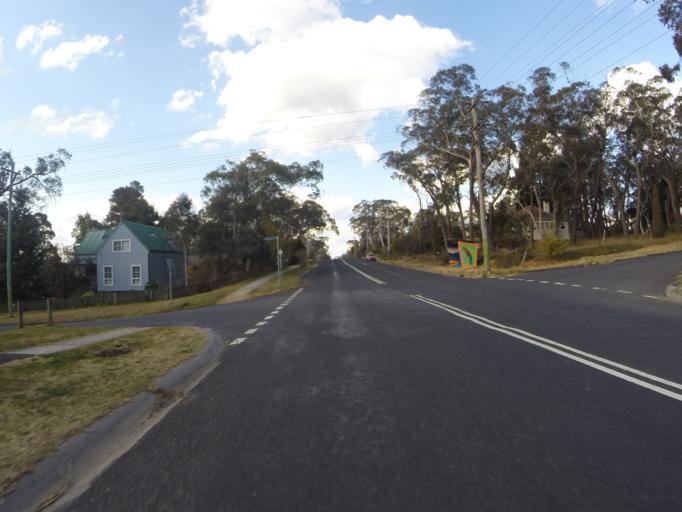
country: AU
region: New South Wales
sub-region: Blue Mountains Municipality
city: Blackheath
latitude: -33.6349
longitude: 150.3006
